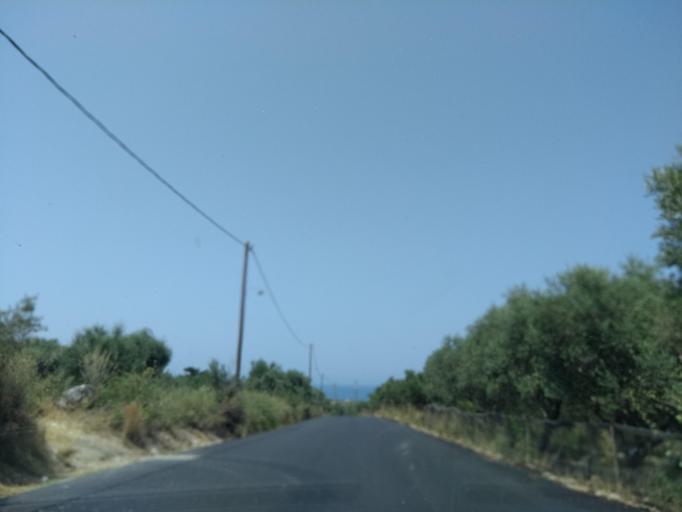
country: GR
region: Crete
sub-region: Nomos Chanias
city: Georgioupolis
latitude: 35.3339
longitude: 24.3017
